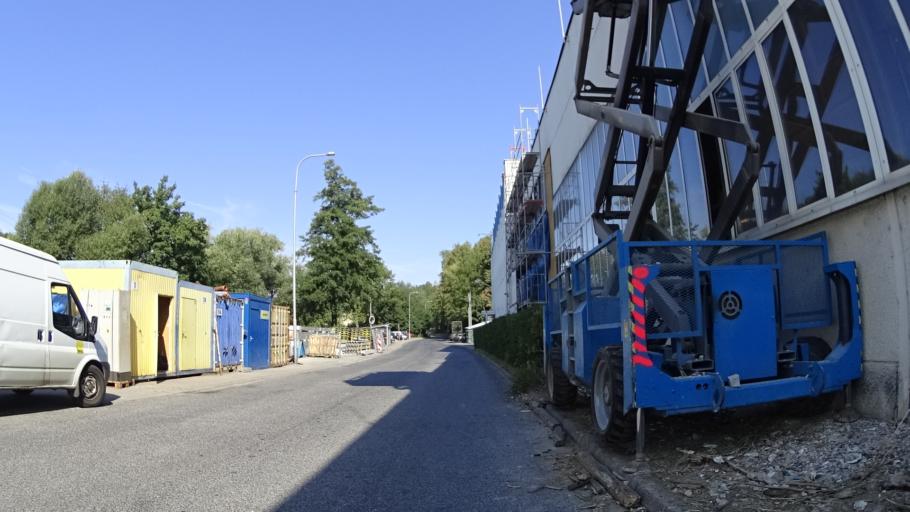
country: CZ
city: Straz nad Nisou
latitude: 50.7880
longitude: 15.0230
